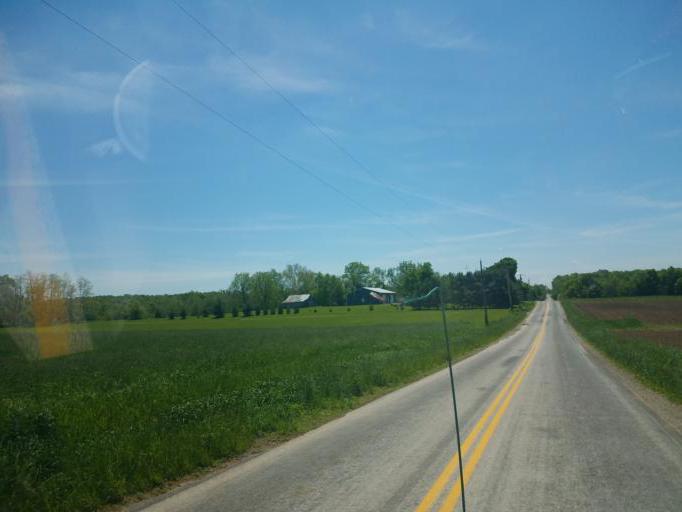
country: US
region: Ohio
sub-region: Ashland County
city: Ashland
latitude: 40.9648
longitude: -82.2437
